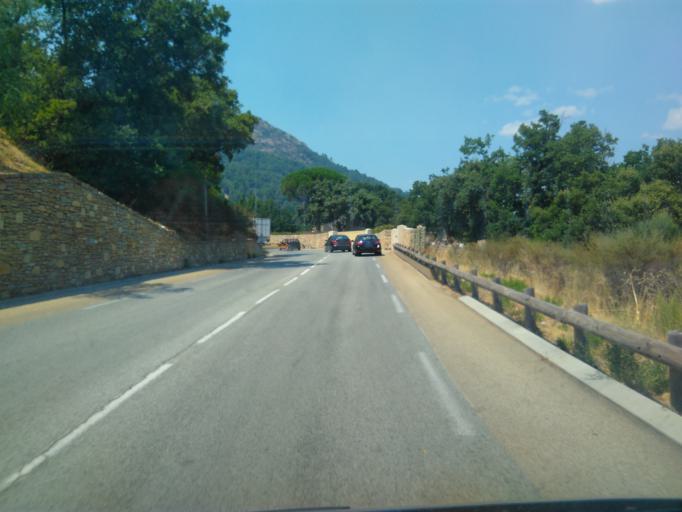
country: FR
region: Provence-Alpes-Cote d'Azur
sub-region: Departement du Var
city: La Garde-Freinet
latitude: 43.3041
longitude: 6.4702
